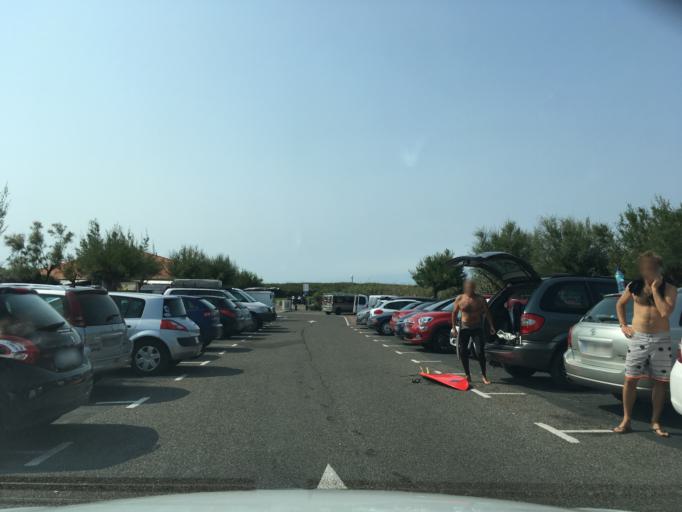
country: FR
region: Aquitaine
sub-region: Departement des Pyrenees-Atlantiques
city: Anglet
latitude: 43.5207
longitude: -1.5244
